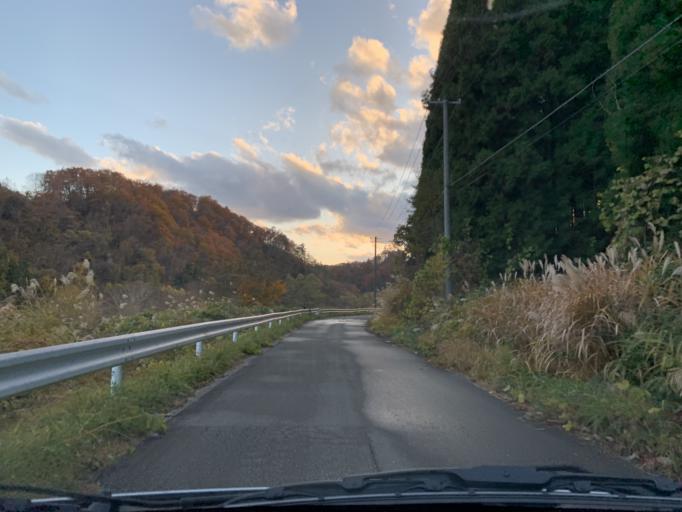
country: JP
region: Iwate
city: Ichinoseki
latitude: 39.0221
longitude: 141.0282
